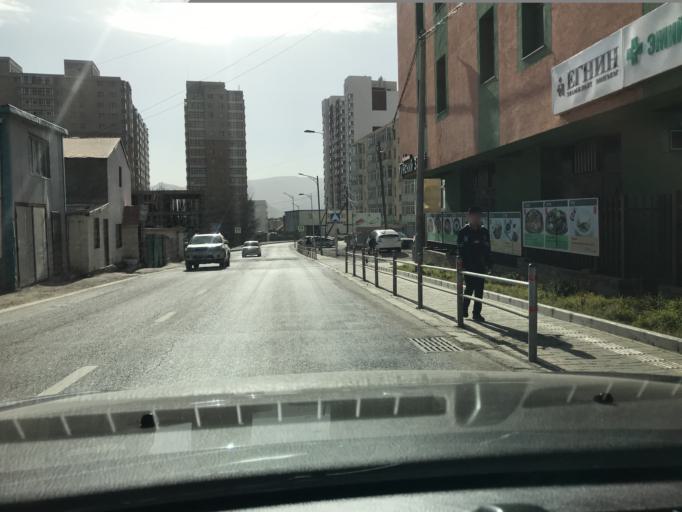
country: MN
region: Ulaanbaatar
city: Ulaanbaatar
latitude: 47.9220
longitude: 106.9608
